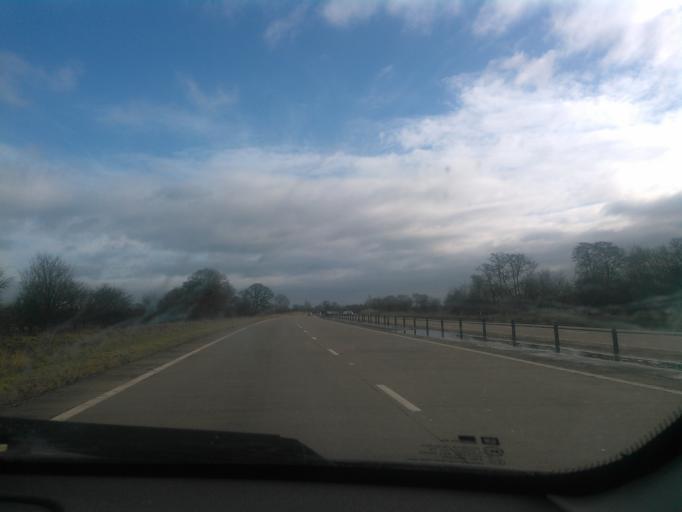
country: GB
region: England
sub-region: Staffordshire
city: Uttoxeter
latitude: 52.9015
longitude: -1.8002
